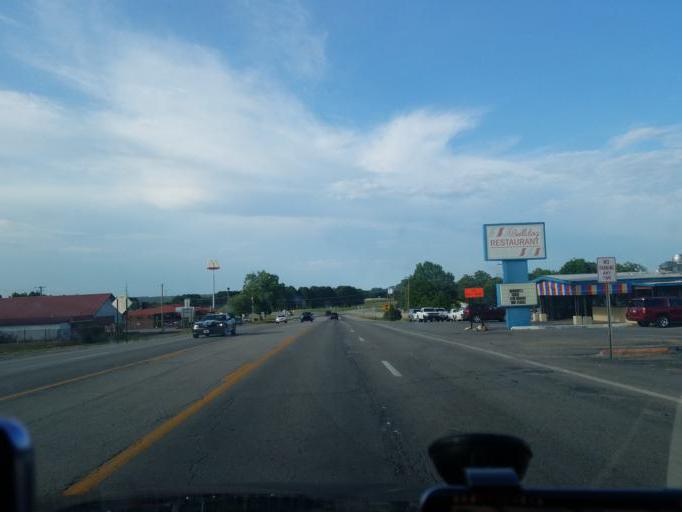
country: US
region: Arkansas
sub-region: White County
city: Bald Knob
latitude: 35.3159
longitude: -91.5635
